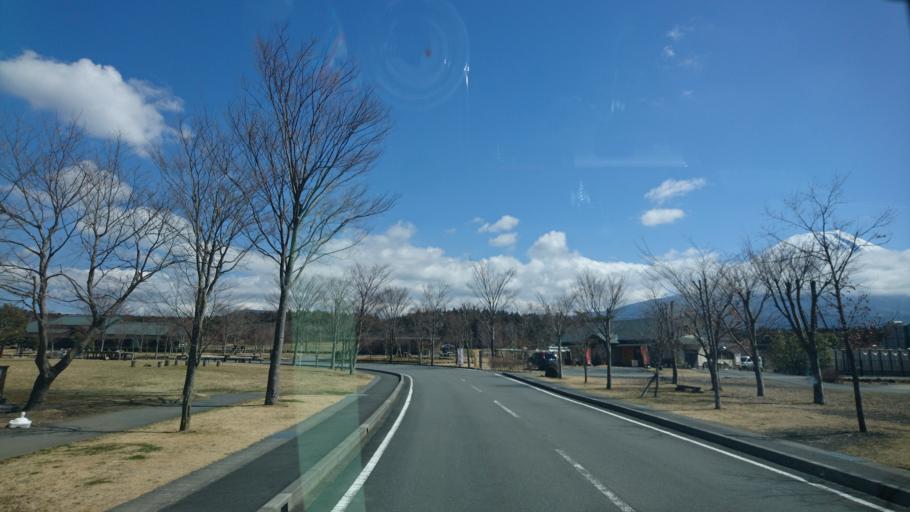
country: JP
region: Yamanashi
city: Fujikawaguchiko
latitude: 35.4119
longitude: 138.5909
